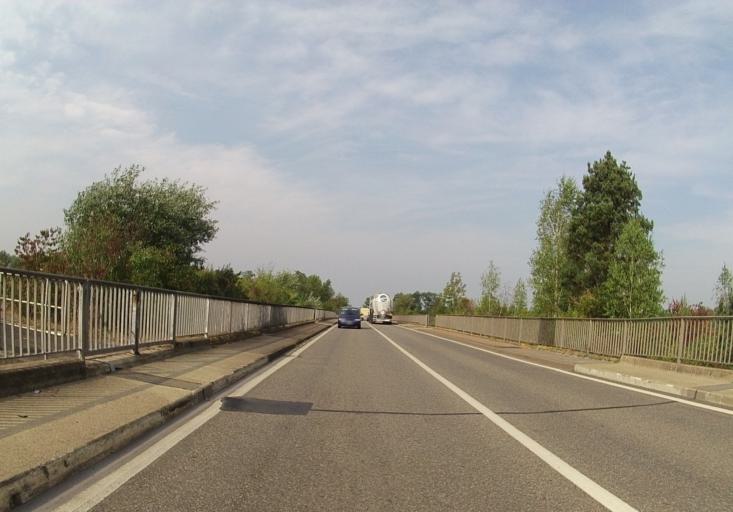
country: DE
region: Baden-Wuerttemberg
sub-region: Karlsruhe Region
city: Hugelsheim
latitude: 48.8338
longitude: 8.1032
